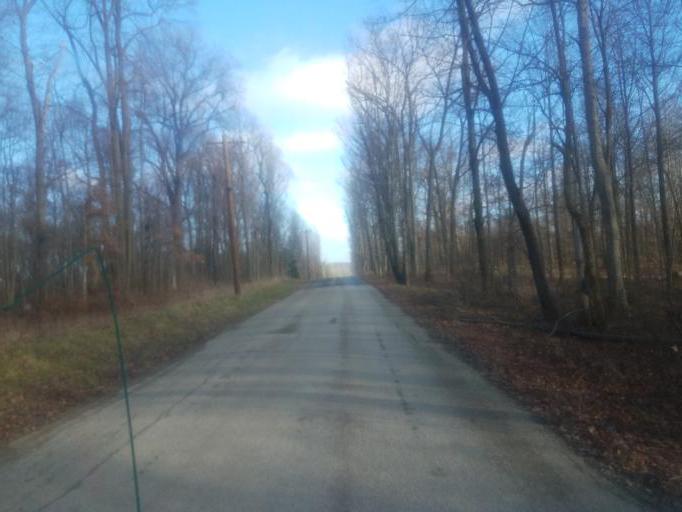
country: US
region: Ohio
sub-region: Sandusky County
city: Bellville
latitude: 40.5801
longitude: -82.4634
